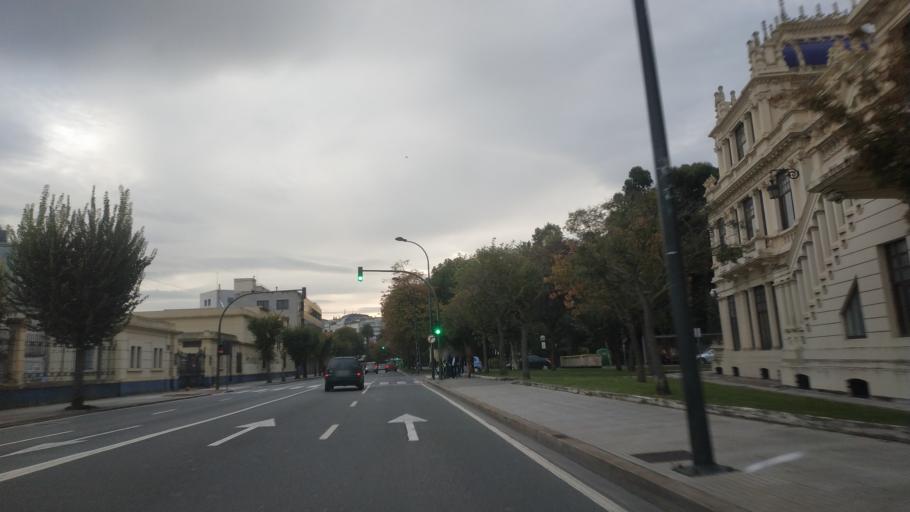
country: ES
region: Galicia
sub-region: Provincia da Coruna
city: A Coruna
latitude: 43.3676
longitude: -8.4020
